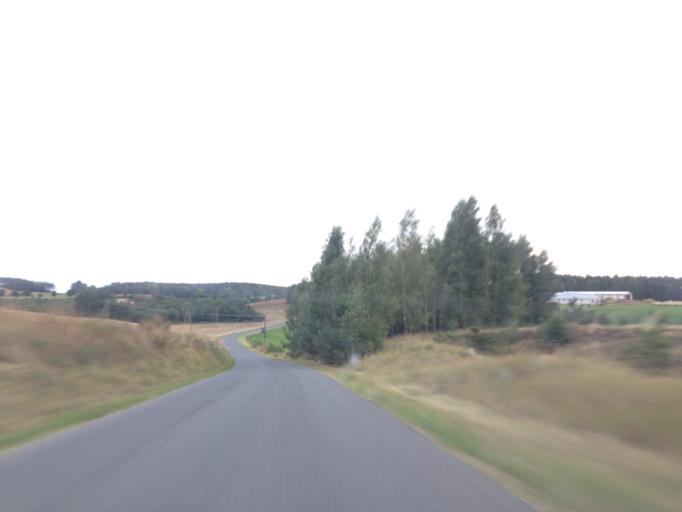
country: PL
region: Kujawsko-Pomorskie
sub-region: Powiat brodnicki
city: Brzozie
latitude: 53.2979
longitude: 19.6875
